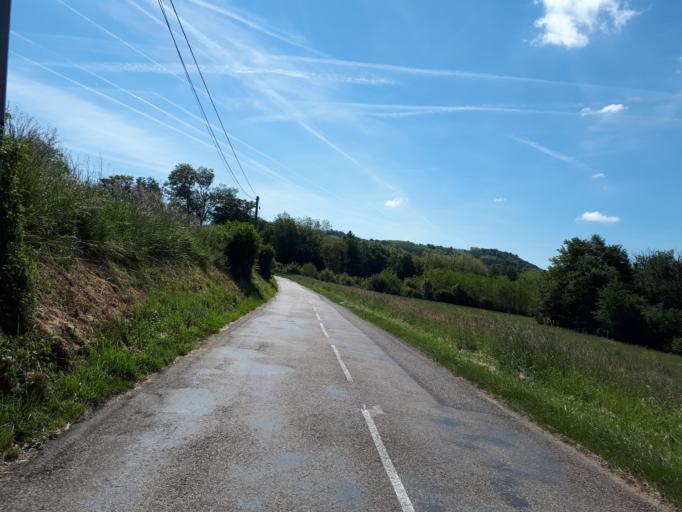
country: FR
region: Rhone-Alpes
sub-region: Departement de l'Isere
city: Ruy
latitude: 45.6001
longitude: 5.3494
